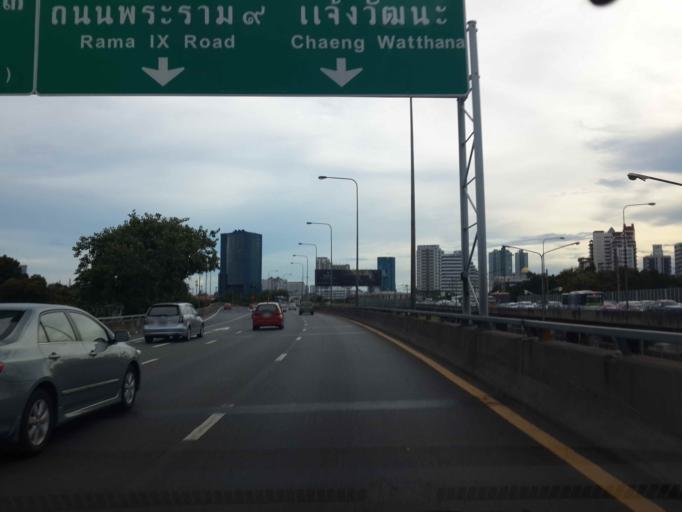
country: TH
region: Bangkok
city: Yan Nawa
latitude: 13.7078
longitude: 100.5488
